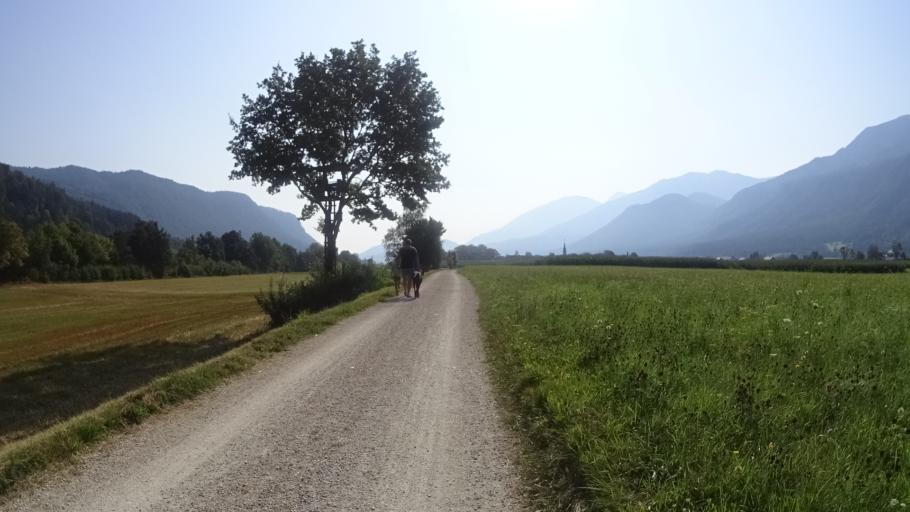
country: AT
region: Carinthia
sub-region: Politischer Bezirk Klagenfurt Land
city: Ferlach
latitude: 46.5453
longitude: 14.3268
